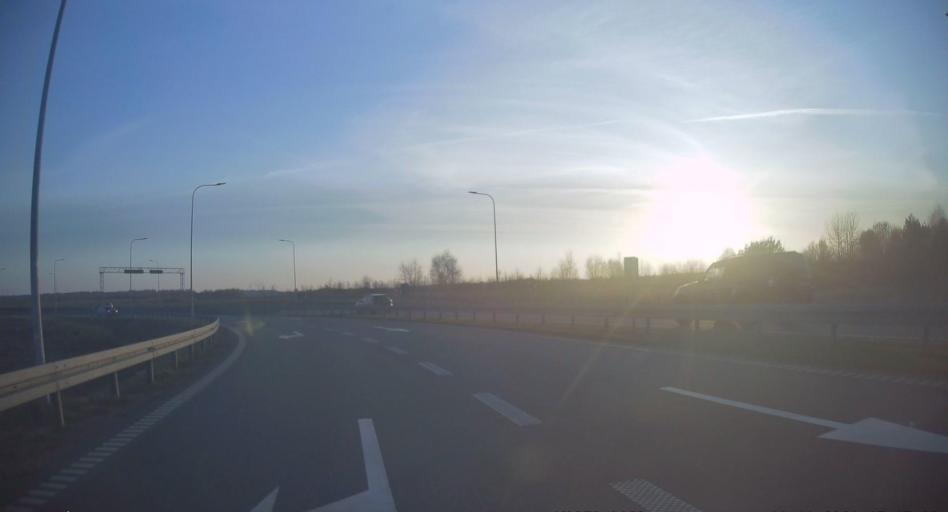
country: PL
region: Silesian Voivodeship
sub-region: Powiat klobucki
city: Kamyk
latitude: 50.8506
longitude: 19.0356
